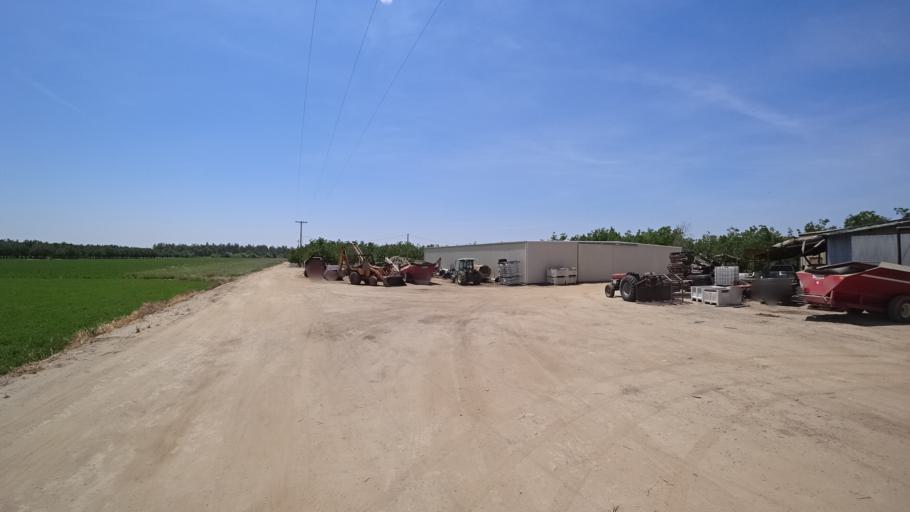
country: US
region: California
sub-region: Fresno County
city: Riverdale
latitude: 36.3897
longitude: -119.8163
